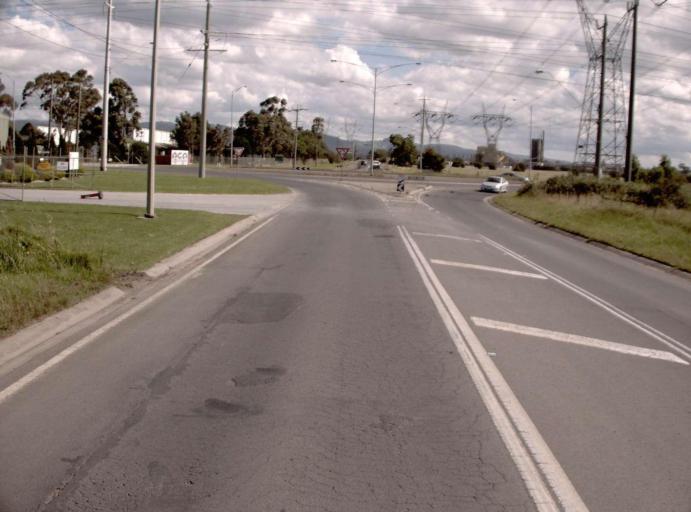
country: AU
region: Victoria
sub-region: Latrobe
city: Morwell
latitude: -38.2475
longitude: 146.4363
